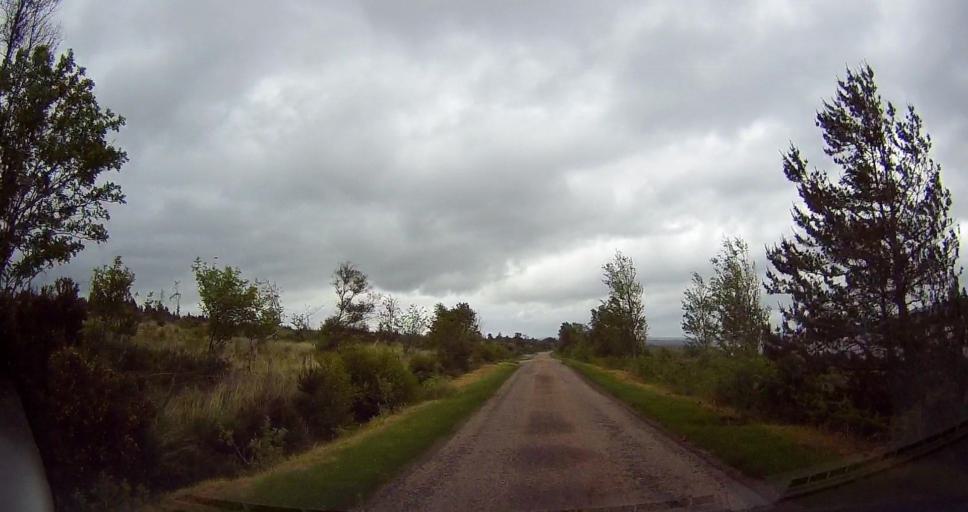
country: GB
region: Scotland
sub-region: Highland
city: Evanton
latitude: 58.0693
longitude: -4.4560
